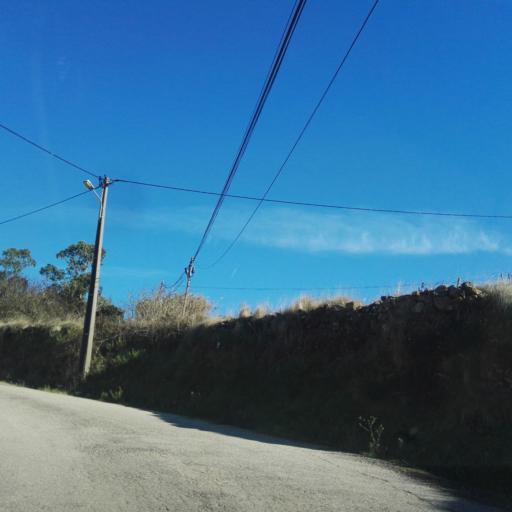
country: PT
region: Lisbon
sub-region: Mafra
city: Milharado
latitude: 38.9702
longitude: -9.1924
